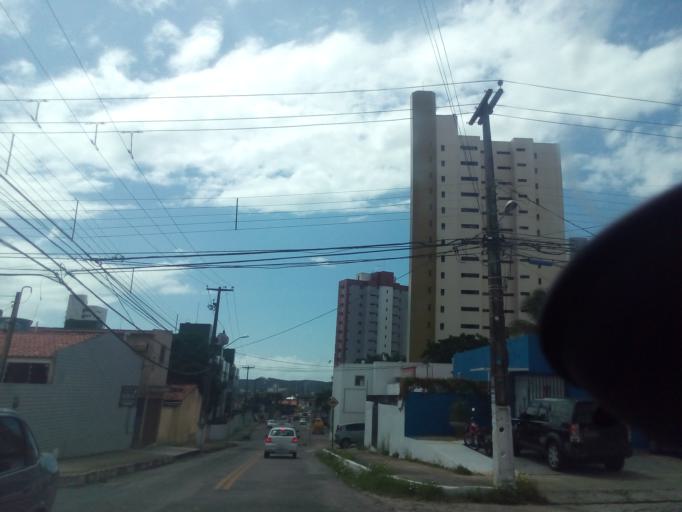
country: BR
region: Rio Grande do Norte
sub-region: Natal
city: Natal
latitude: -5.8391
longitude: -35.2158
